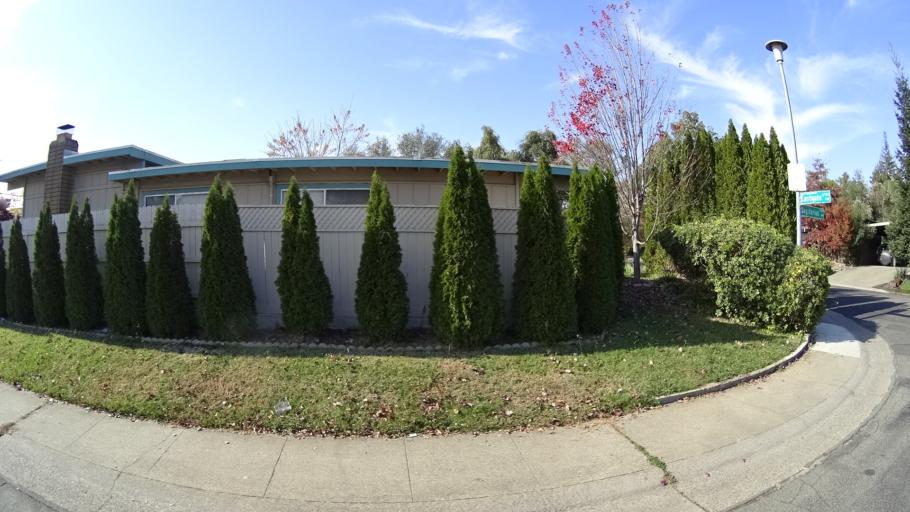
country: US
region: California
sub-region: Sacramento County
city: Fair Oaks
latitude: 38.6673
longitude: -121.2827
